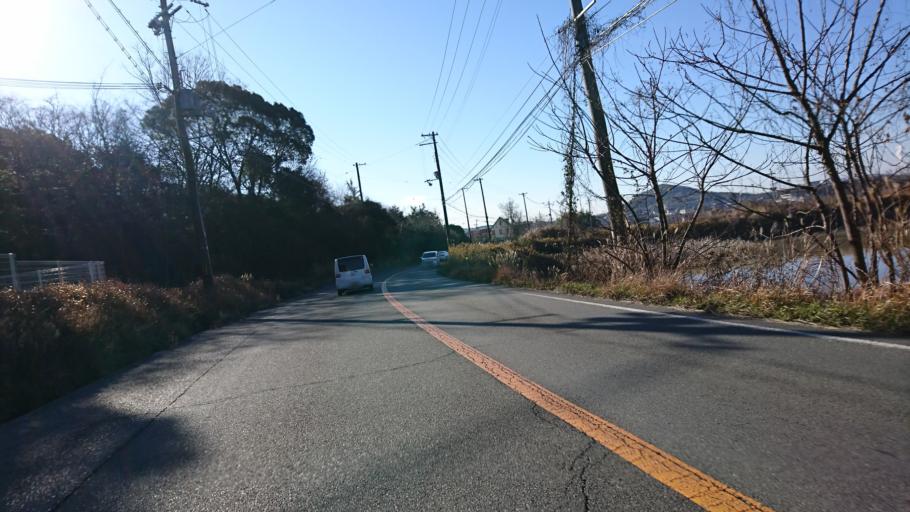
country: JP
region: Hyogo
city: Kakogawacho-honmachi
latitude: 34.8201
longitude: 134.8356
